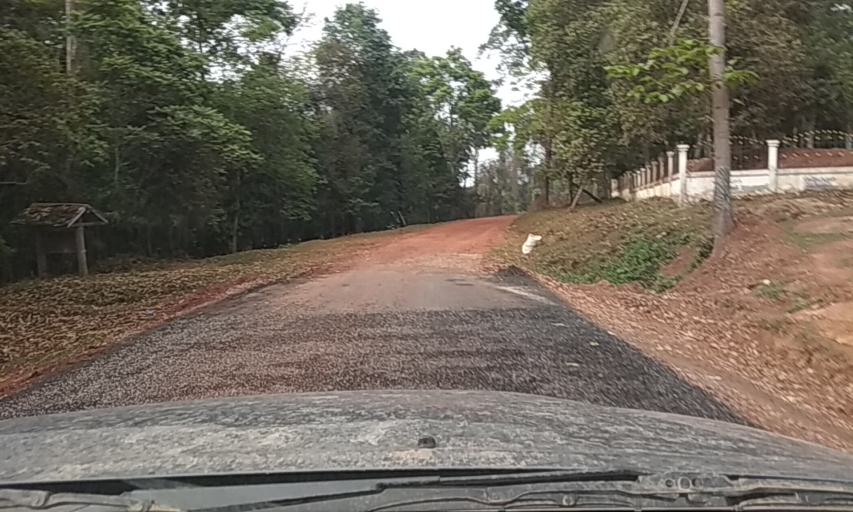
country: TH
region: Nan
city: Mae Charim
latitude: 18.4089
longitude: 101.1732
